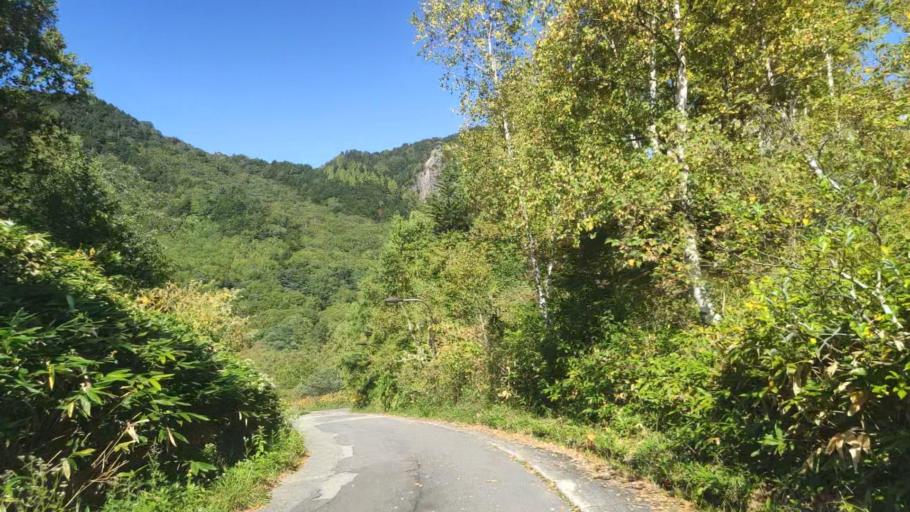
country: JP
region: Nagano
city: Nakano
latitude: 36.6975
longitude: 138.4886
